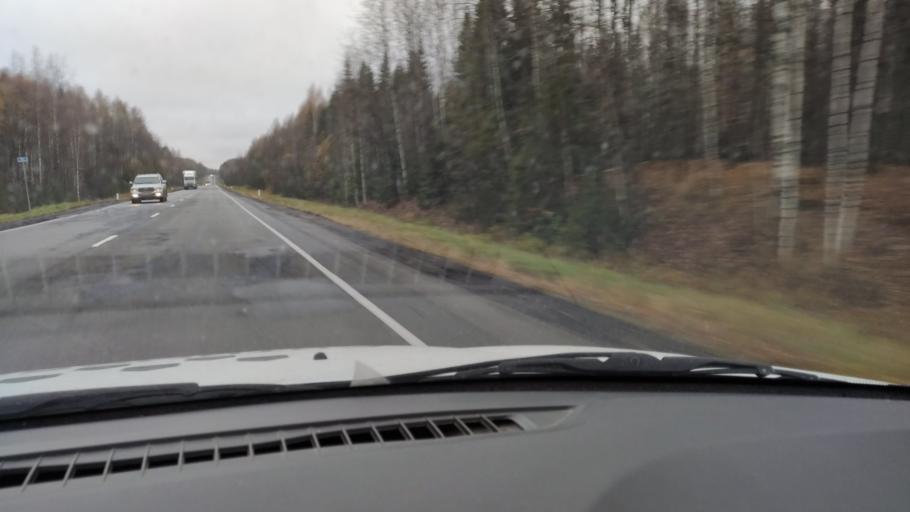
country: RU
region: Kirov
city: Chernaya Kholunitsa
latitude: 58.7708
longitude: 51.9565
